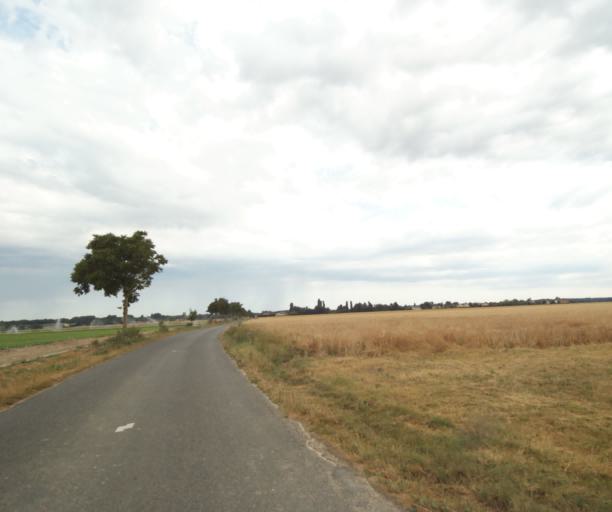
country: FR
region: Ile-de-France
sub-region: Departement de Seine-et-Marne
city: Arbonne-la-Foret
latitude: 48.4298
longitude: 2.5598
